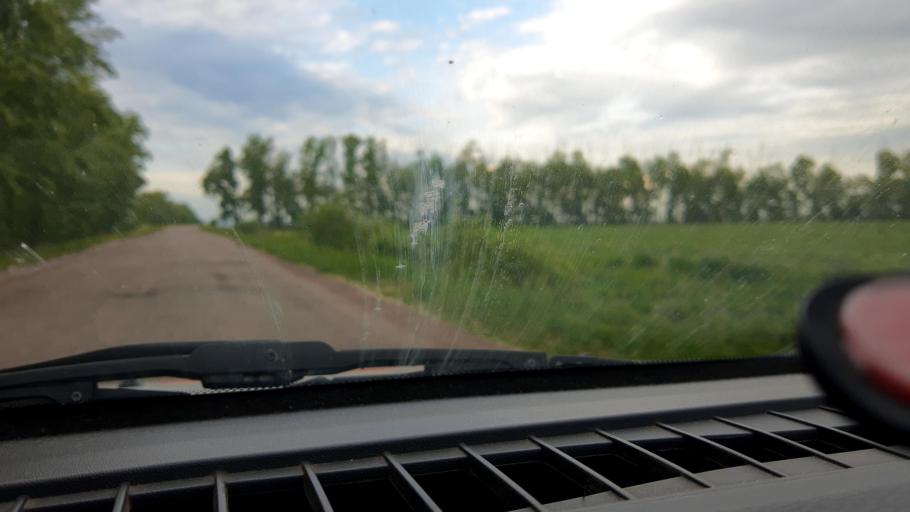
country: RU
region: Bashkortostan
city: Asanovo
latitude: 54.8304
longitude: 55.5990
